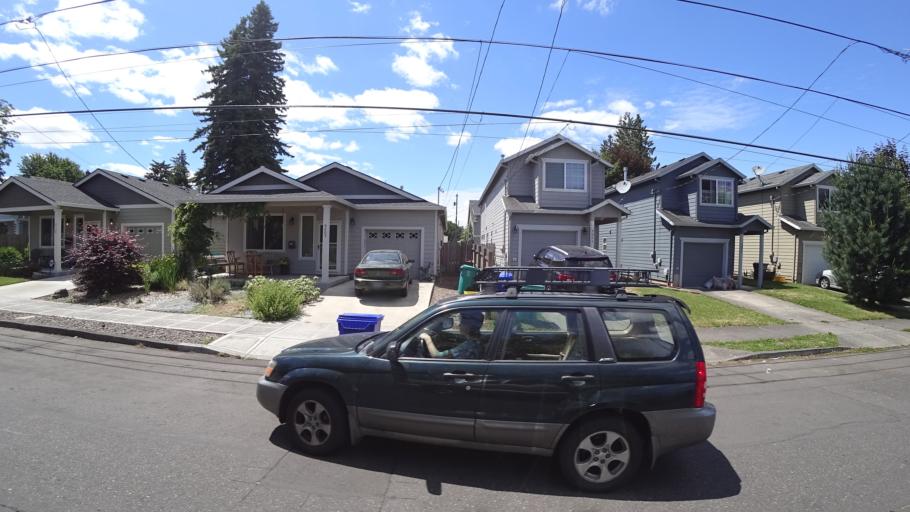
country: US
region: Washington
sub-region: Clark County
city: Vancouver
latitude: 45.5894
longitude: -122.7200
